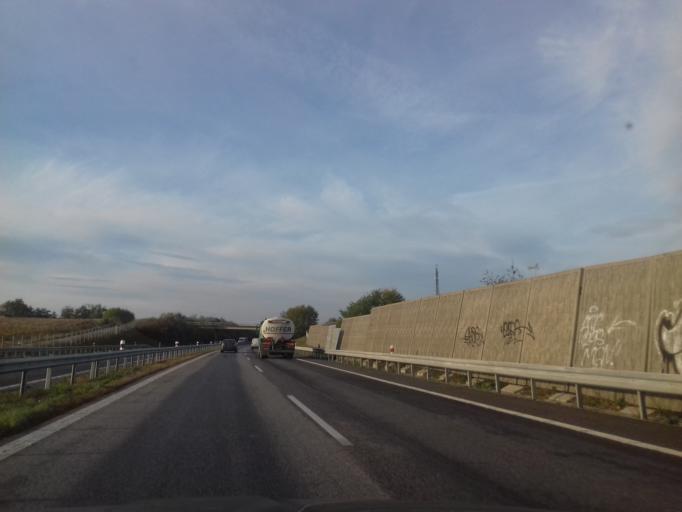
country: SK
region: Nitriansky
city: Sellye
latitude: 48.2722
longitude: 17.8384
